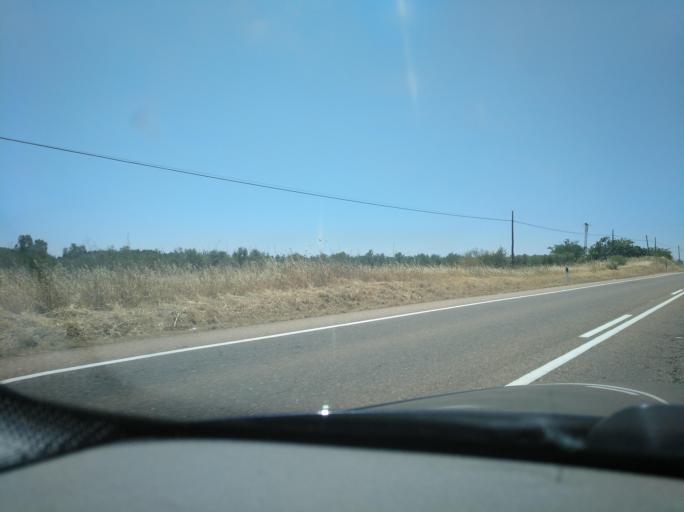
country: ES
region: Extremadura
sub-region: Provincia de Badajoz
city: Olivenza
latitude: 38.7334
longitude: -7.0697
